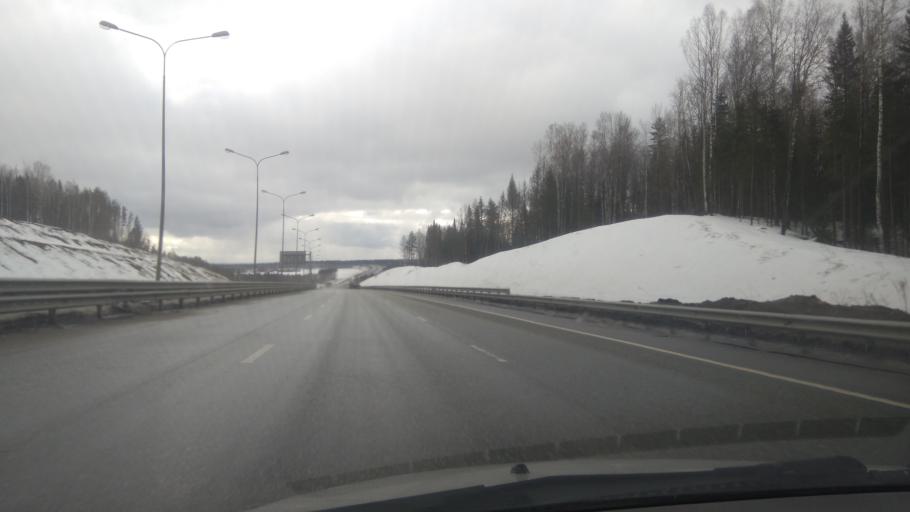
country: RU
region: Perm
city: Bershet'
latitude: 57.7293
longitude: 56.3485
